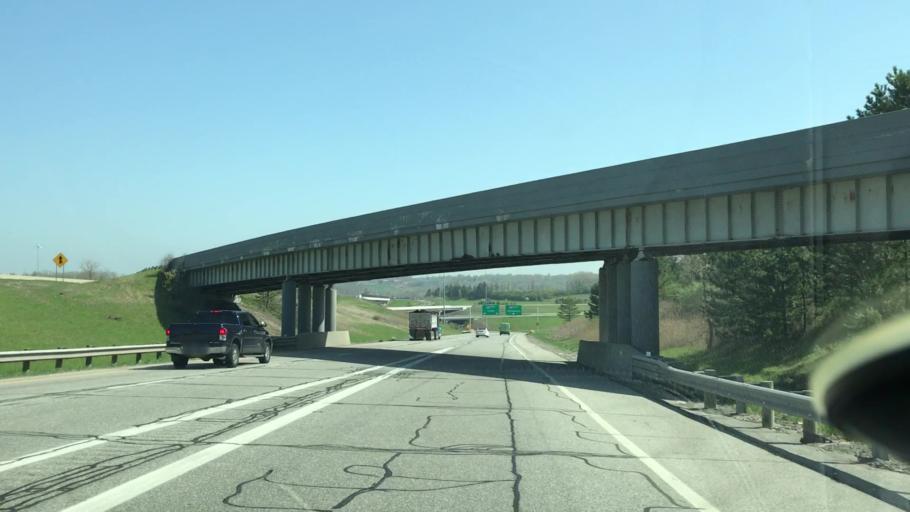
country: US
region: Ohio
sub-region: Cuyahoga County
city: Seven Hills
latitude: 41.4018
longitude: -81.6494
